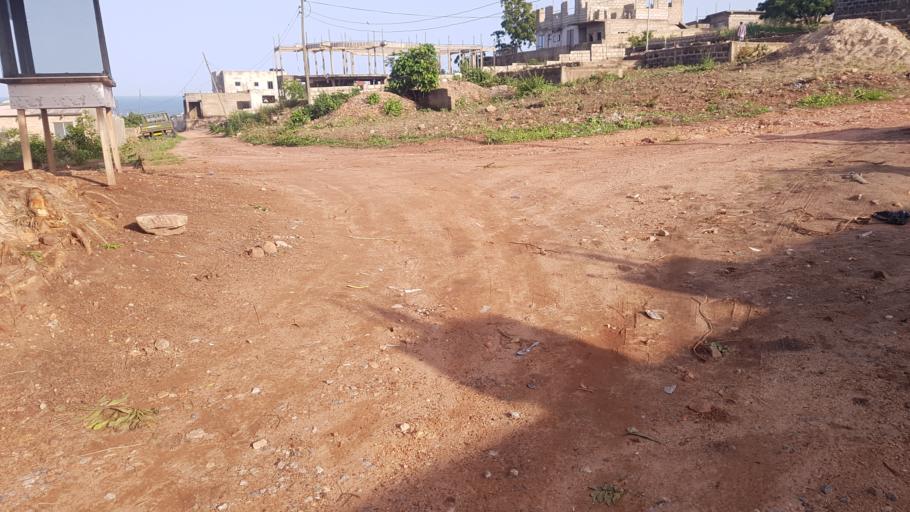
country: GH
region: Greater Accra
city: Gbawe
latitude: 5.5194
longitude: -0.3383
